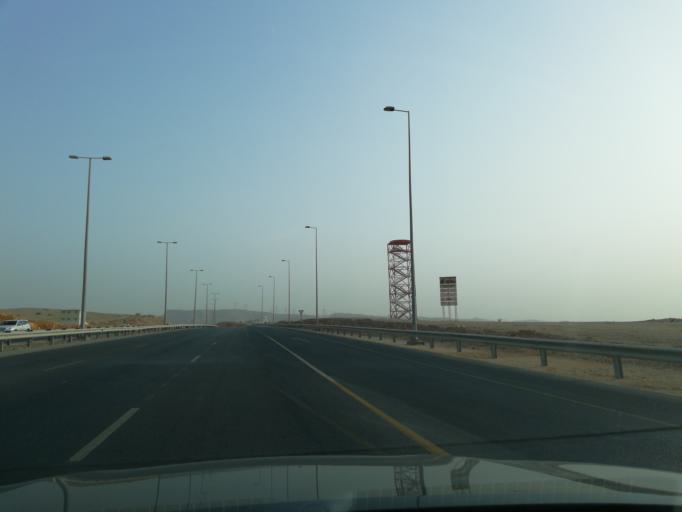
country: OM
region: Muhafazat Masqat
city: Bawshar
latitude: 23.5679
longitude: 58.2928
